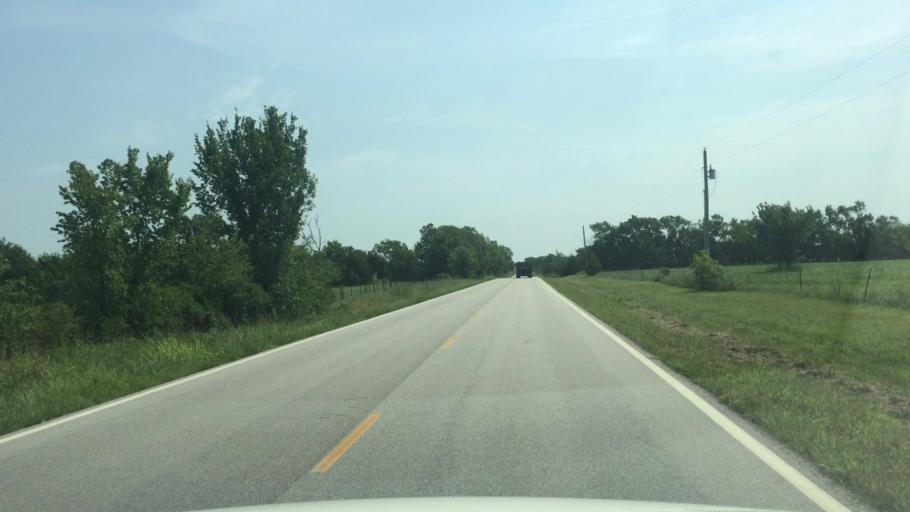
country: US
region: Kansas
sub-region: Montgomery County
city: Cherryvale
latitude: 37.1940
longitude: -95.5466
